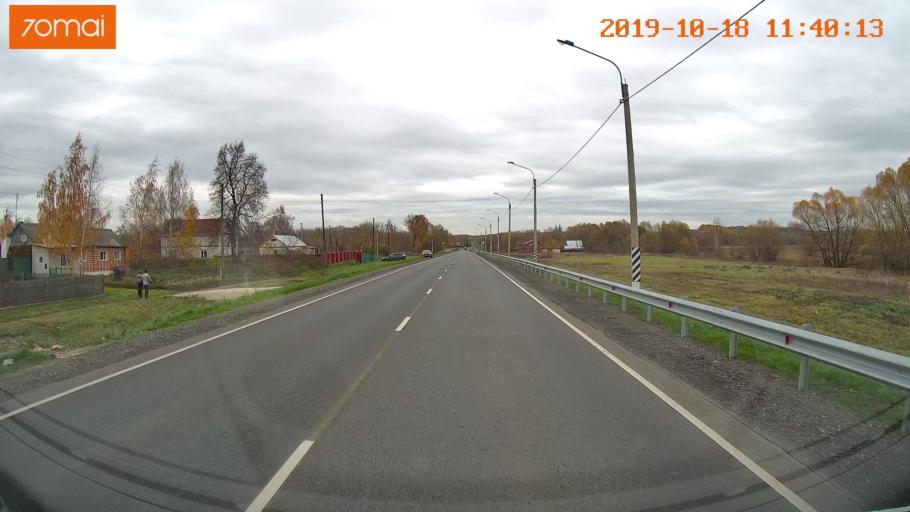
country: RU
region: Rjazan
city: Oktyabr'skiy
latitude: 54.1783
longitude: 38.8876
